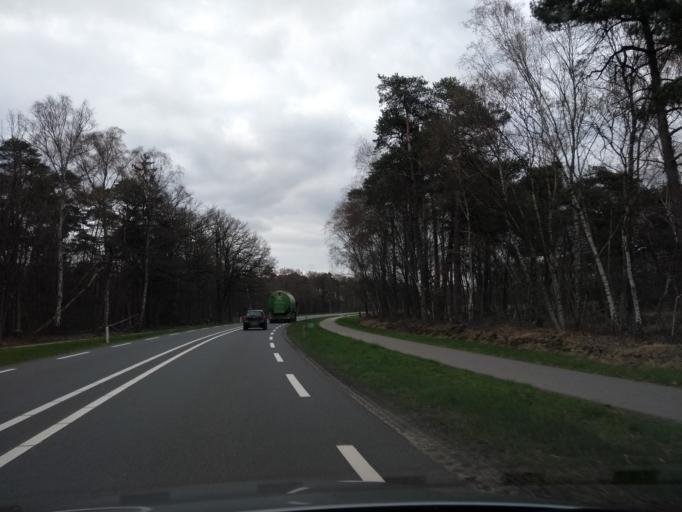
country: NL
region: Overijssel
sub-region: Gemeente Haaksbergen
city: Haaksbergen
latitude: 52.2037
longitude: 6.7301
